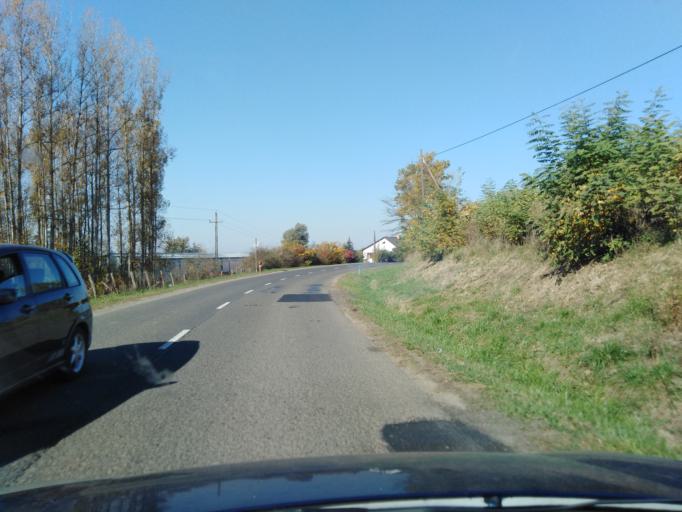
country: HU
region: Nograd
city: Karancskeszi
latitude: 48.1555
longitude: 19.7101
